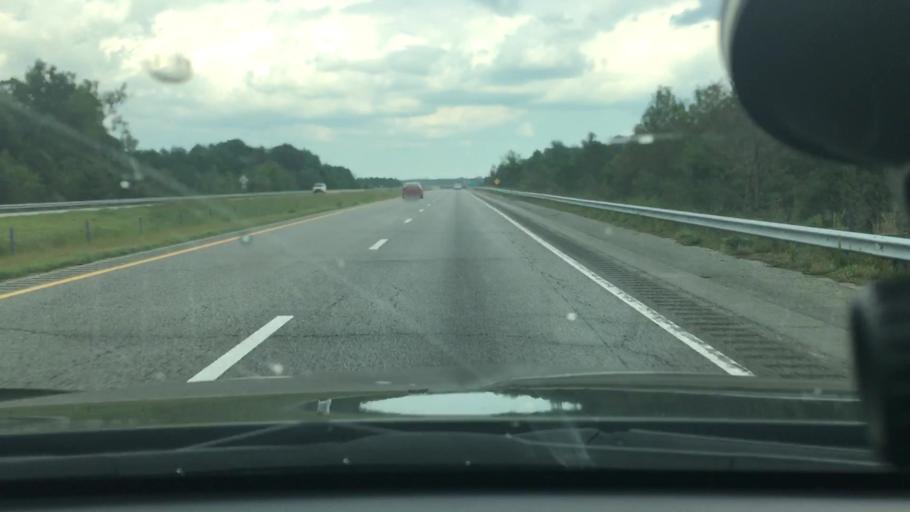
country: US
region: North Carolina
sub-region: Wilson County
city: Wilson
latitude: 35.6742
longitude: -77.9159
